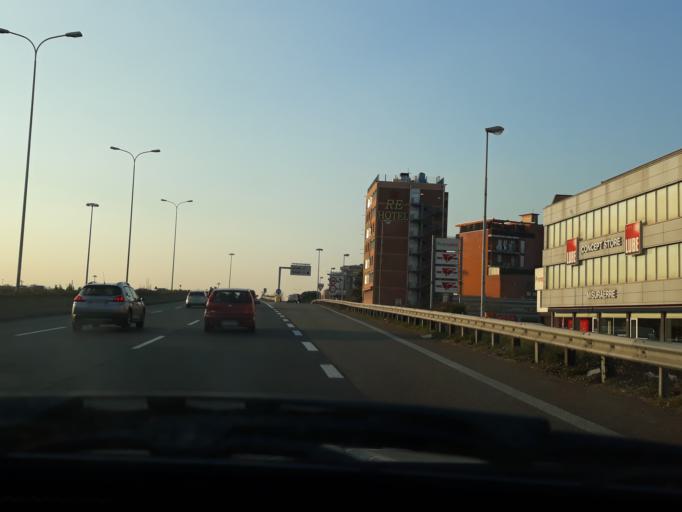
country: IT
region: Lombardy
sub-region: Provincia di Monza e Brianza
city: Lissone
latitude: 45.5992
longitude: 9.2381
